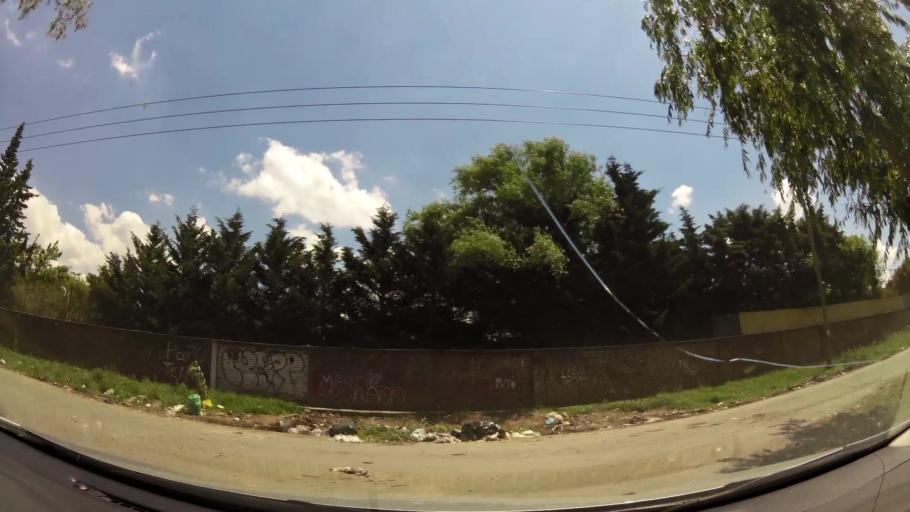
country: AR
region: Buenos Aires
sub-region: Partido de Tigre
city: Tigre
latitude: -34.4307
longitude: -58.5988
